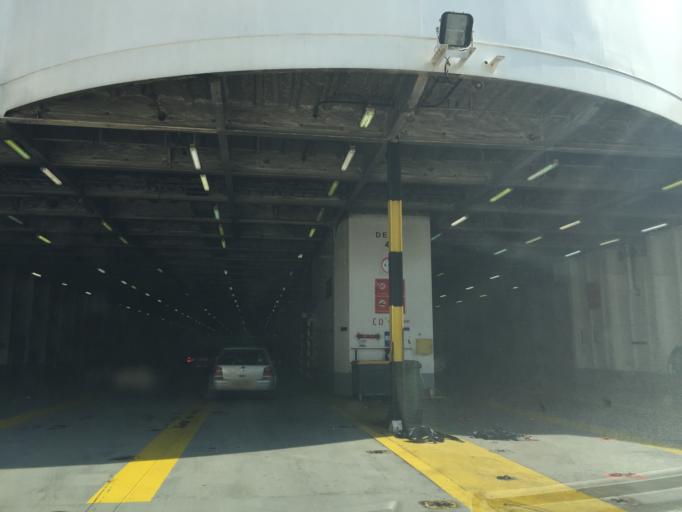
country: GB
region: England
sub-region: Kent
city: Dover
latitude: 51.1270
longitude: 1.3380
